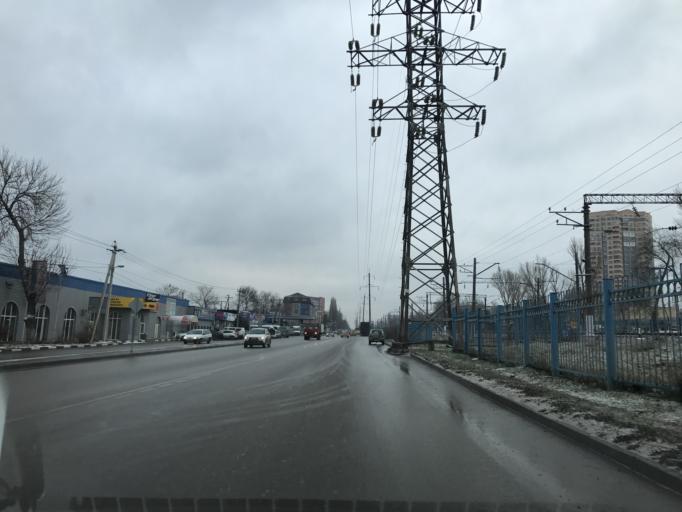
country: RU
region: Rostov
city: Rostov-na-Donu
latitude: 47.2452
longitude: 39.6973
